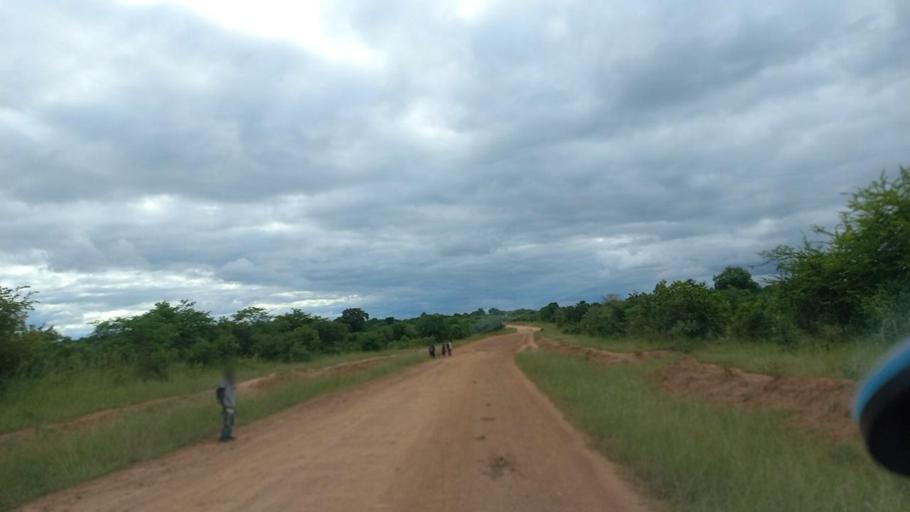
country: ZM
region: Lusaka
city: Chongwe
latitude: -15.4501
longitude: 28.8439
